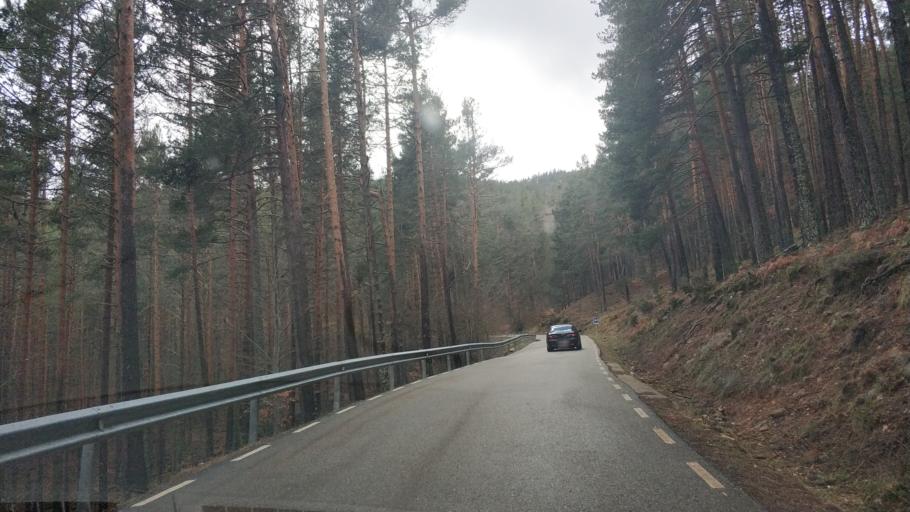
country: ES
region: Castille and Leon
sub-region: Provincia de Burgos
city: Neila
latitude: 42.0490
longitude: -3.0117
